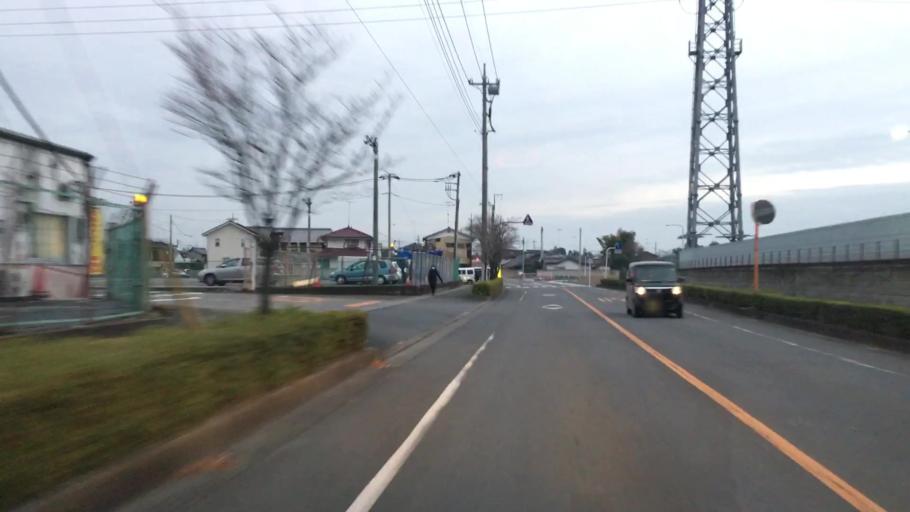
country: JP
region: Gunma
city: Ota
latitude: 36.3020
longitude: 139.3890
